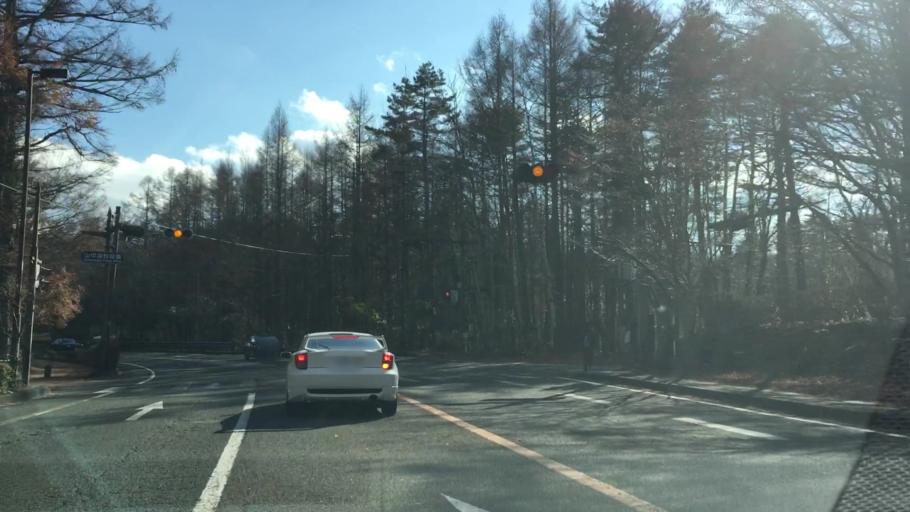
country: JP
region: Shizuoka
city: Gotemba
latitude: 35.4105
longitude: 138.8622
